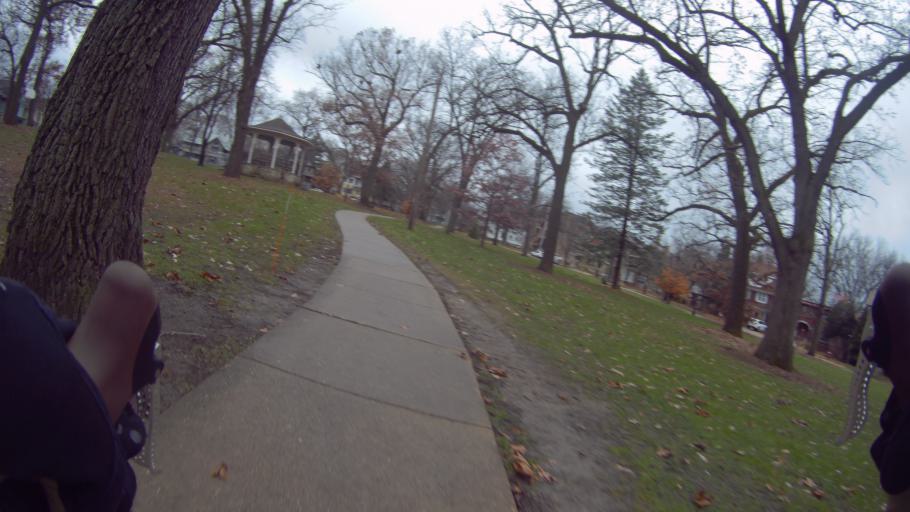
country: US
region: Wisconsin
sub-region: Dane County
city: Monona
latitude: 43.0810
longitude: -89.3630
